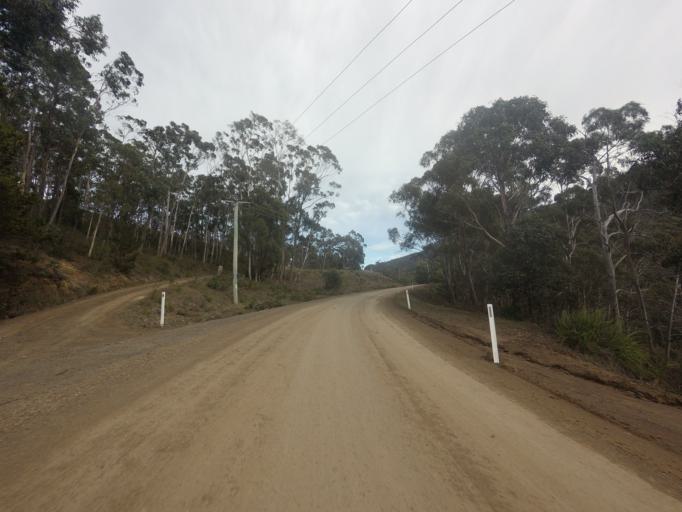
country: AU
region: Tasmania
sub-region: Huon Valley
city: Huonville
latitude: -43.0525
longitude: 147.1061
